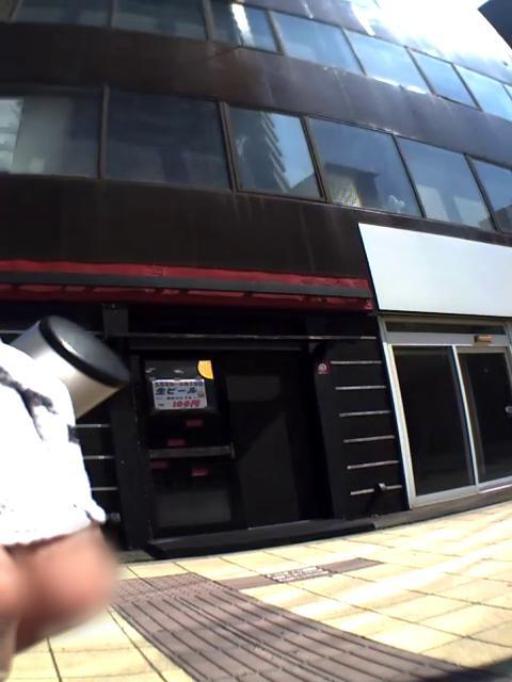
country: JP
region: Osaka
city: Osaka-shi
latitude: 34.6942
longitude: 135.5100
